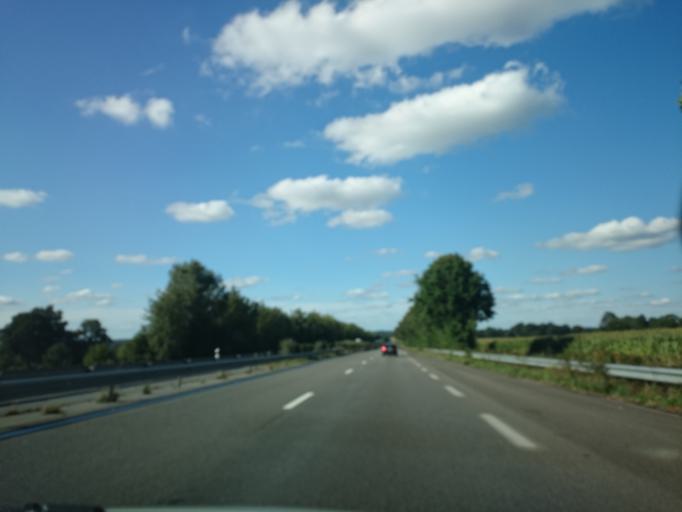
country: FR
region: Pays de la Loire
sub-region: Departement de la Loire-Atlantique
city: Nozay
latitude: 47.5886
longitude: -1.6271
